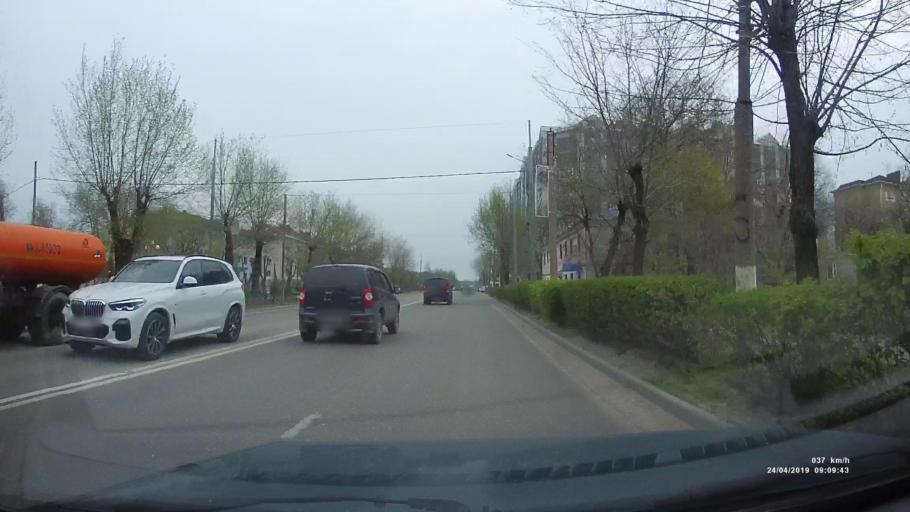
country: RU
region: Kalmykiya
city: Elista
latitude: 46.3091
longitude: 44.2731
